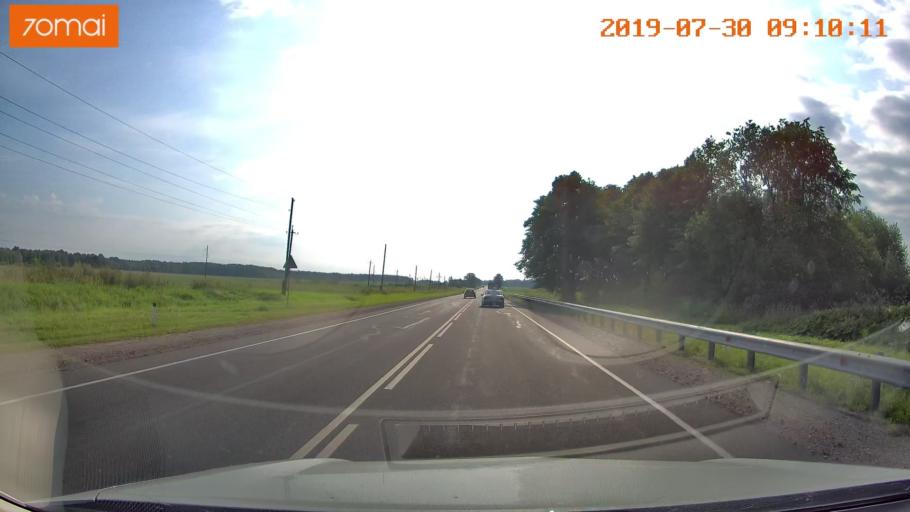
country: RU
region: Kaliningrad
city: Nesterov
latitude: 54.6118
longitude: 22.4215
